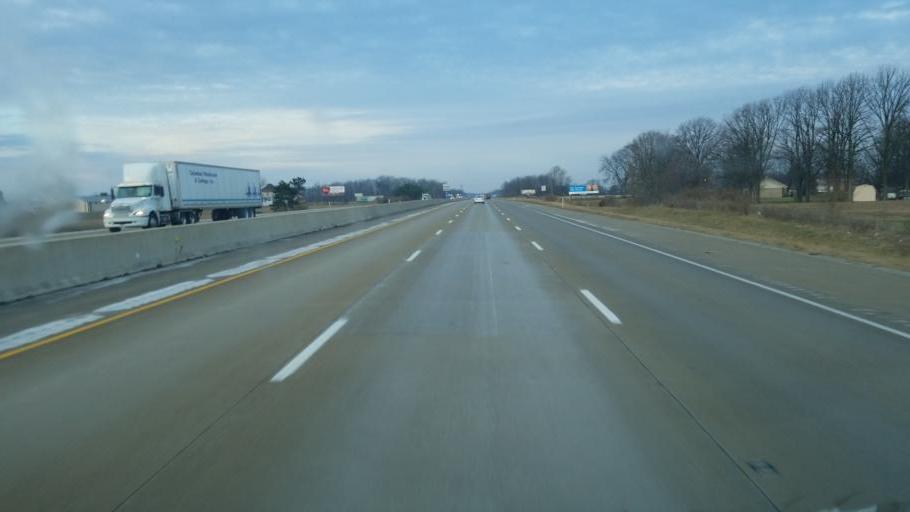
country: US
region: Indiana
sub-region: Marion County
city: Cumberland
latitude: 39.8112
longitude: -85.9400
